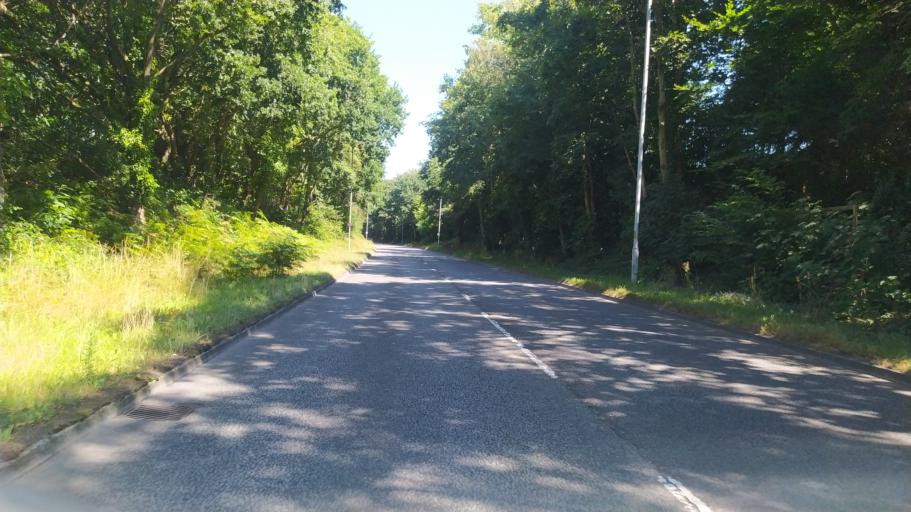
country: GB
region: England
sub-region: Dorset
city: Broadstone
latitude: 50.7543
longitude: -2.0008
